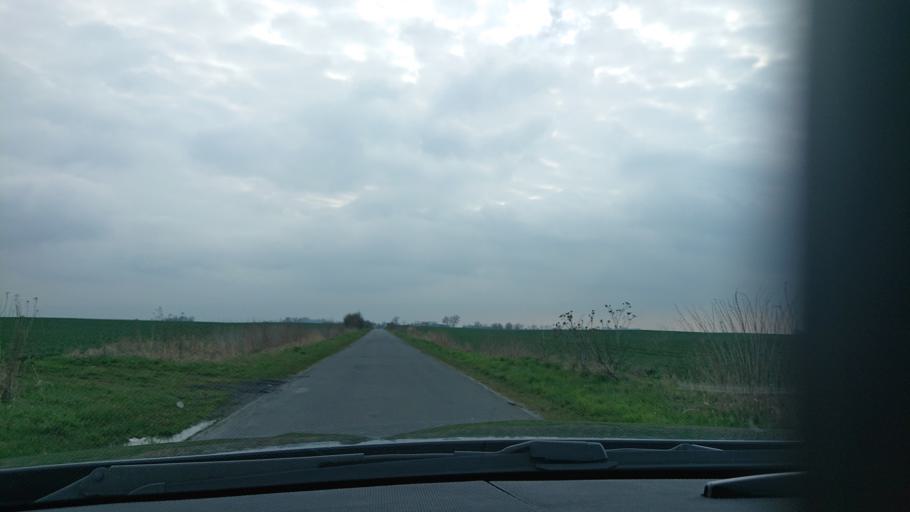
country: PL
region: Greater Poland Voivodeship
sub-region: Powiat gnieznienski
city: Gniezno
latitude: 52.5597
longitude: 17.5188
